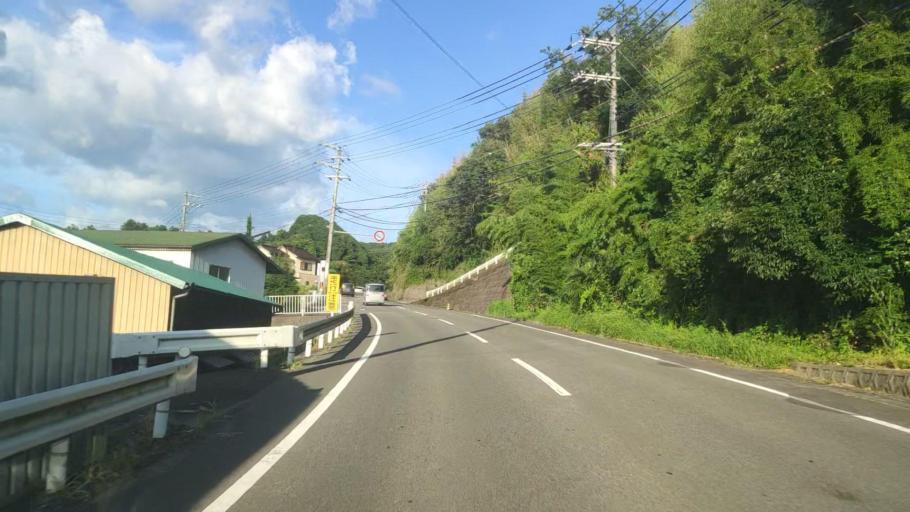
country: JP
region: Wakayama
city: Tanabe
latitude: 33.7346
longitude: 135.4276
